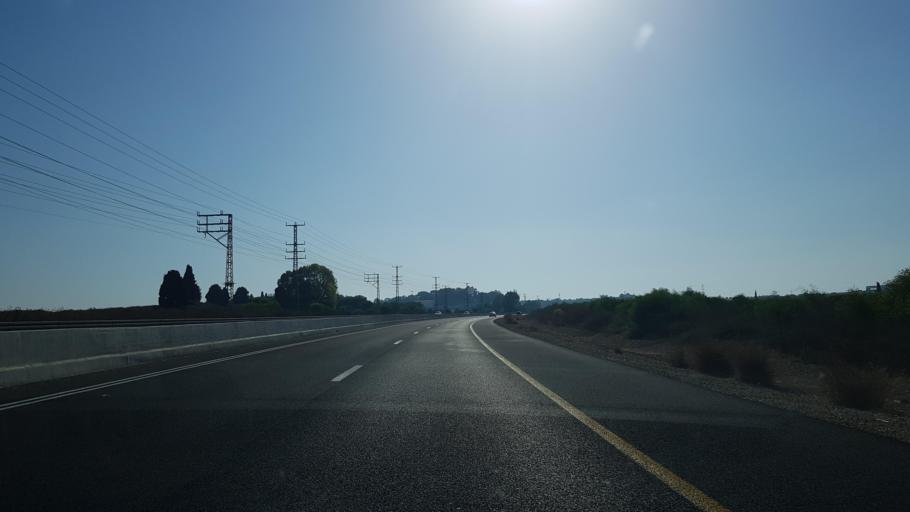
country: IL
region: Southern District
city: Ashqelon
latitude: 31.6879
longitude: 34.6647
